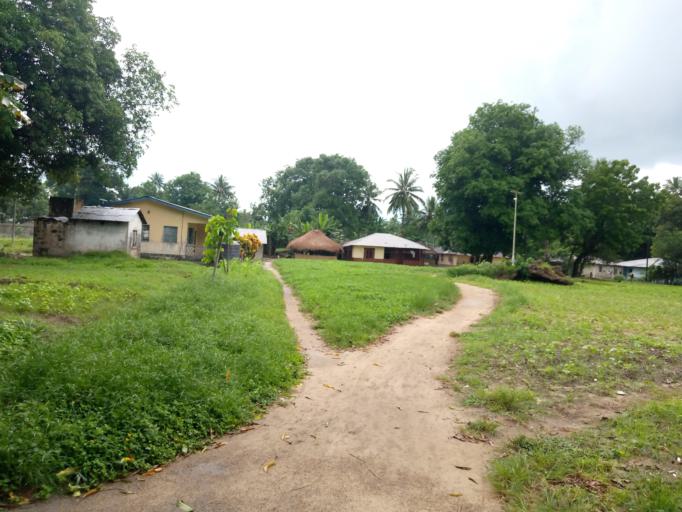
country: SL
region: Southern Province
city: Bonthe
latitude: 7.5322
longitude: -12.5081
